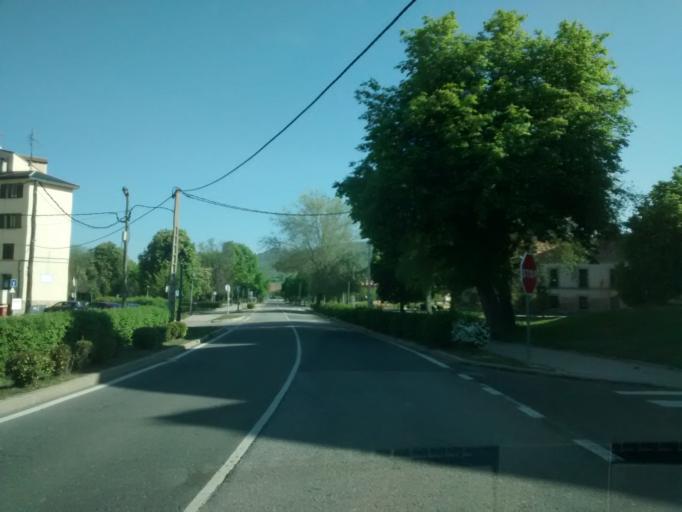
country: ES
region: Castille and Leon
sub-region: Provincia de Segovia
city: San Ildefonso
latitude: 40.9025
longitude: -4.0085
